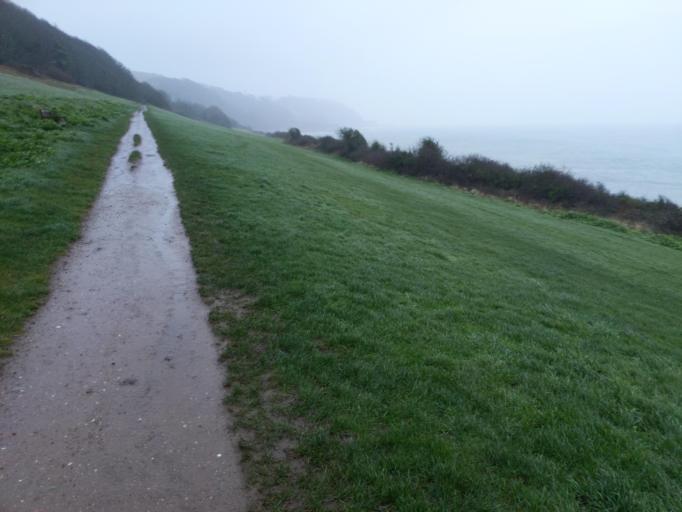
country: GB
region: England
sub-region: Cornwall
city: Millbrook
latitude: 50.3351
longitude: -4.1994
